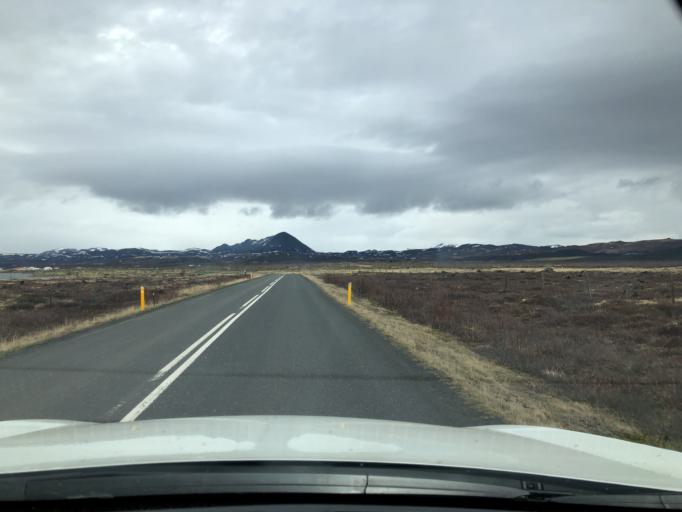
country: IS
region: Northeast
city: Laugar
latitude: 65.6090
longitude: -16.9190
